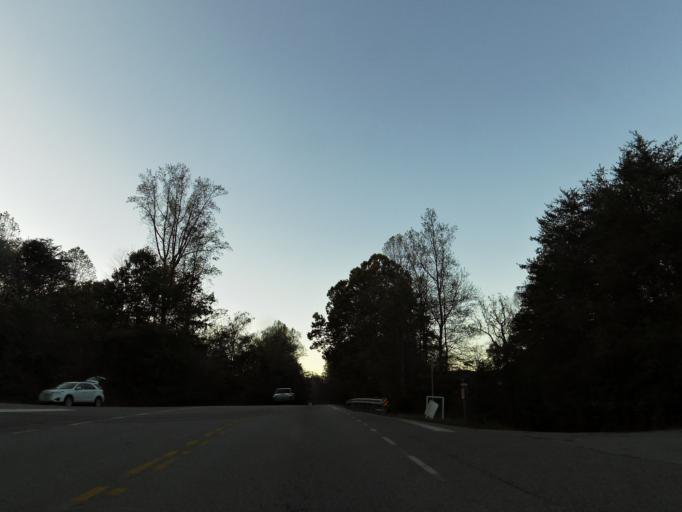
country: US
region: Tennessee
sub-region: Campbell County
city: Caryville
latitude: 36.2688
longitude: -84.1945
